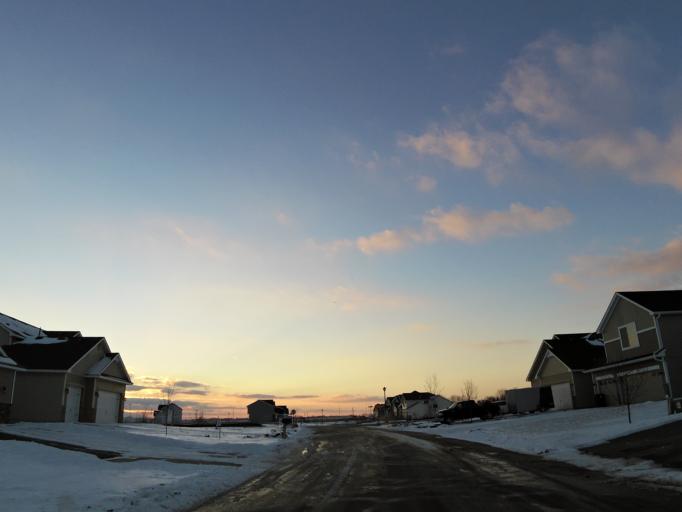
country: US
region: Minnesota
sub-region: Dakota County
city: Farmington
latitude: 44.6731
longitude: -93.1305
